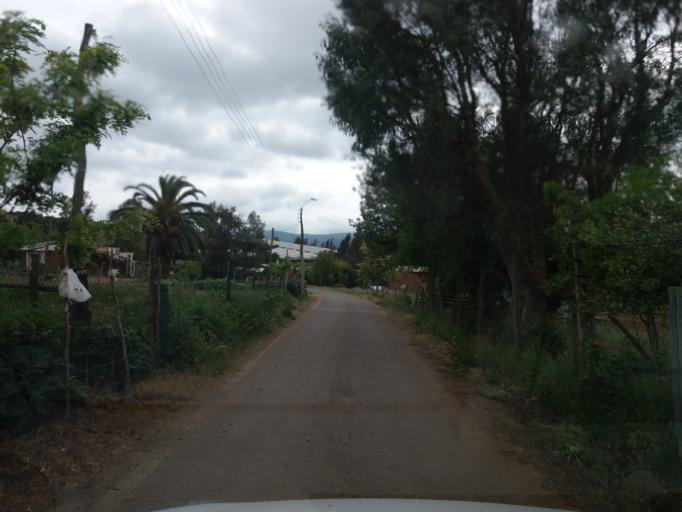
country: CL
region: Valparaiso
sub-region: Provincia de Quillota
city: Quillota
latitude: -32.8949
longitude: -71.3204
